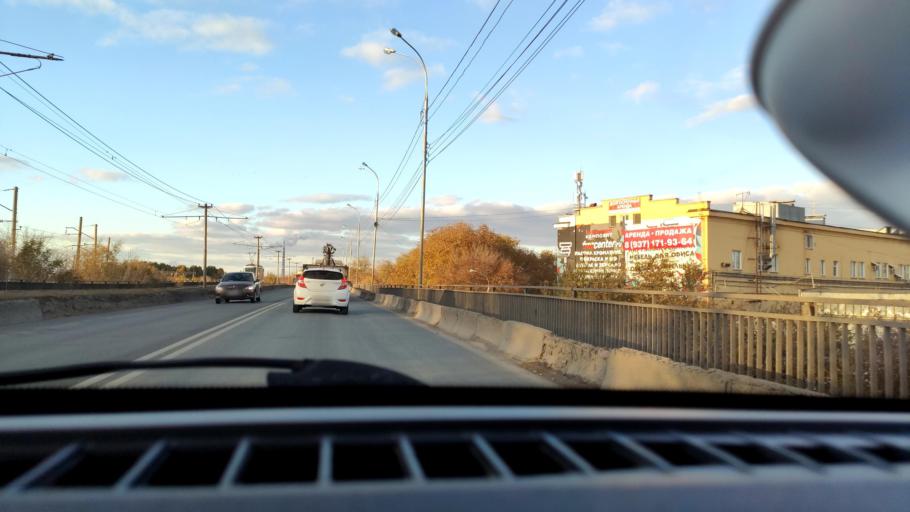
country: RU
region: Samara
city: Smyshlyayevka
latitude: 53.2186
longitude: 50.2904
